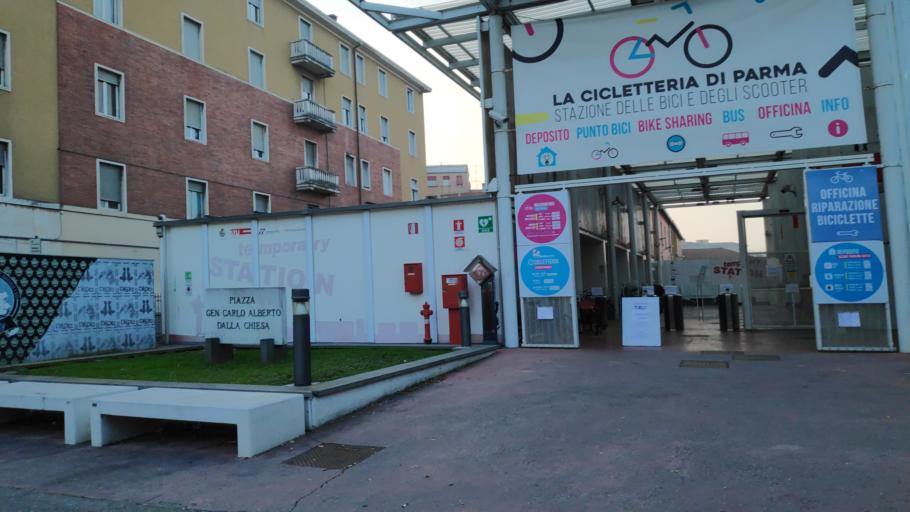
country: IT
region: Emilia-Romagna
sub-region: Provincia di Parma
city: Parma
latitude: 44.8100
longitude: 10.3277
